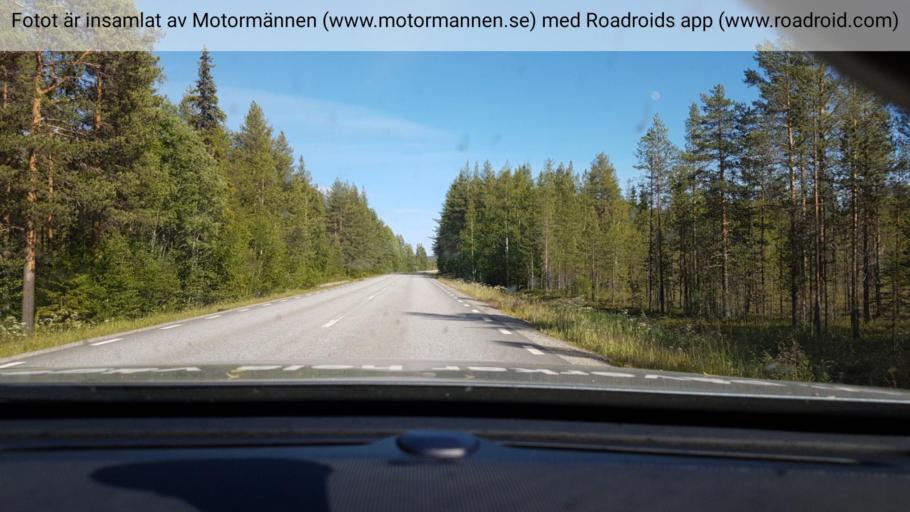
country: SE
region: Vaesterbotten
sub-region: Lycksele Kommun
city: Lycksele
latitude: 64.6458
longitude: 18.4951
